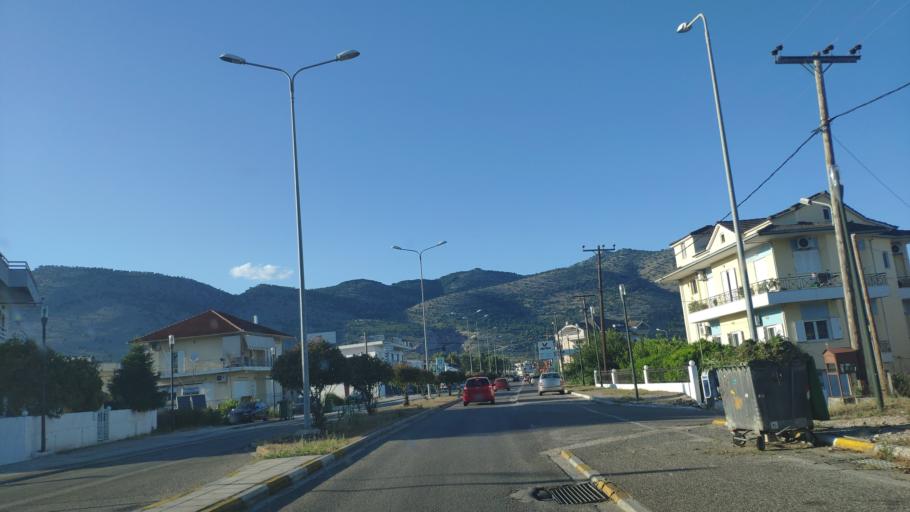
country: GR
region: Epirus
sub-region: Nomos Prevezis
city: Louros
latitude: 39.1603
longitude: 20.7538
